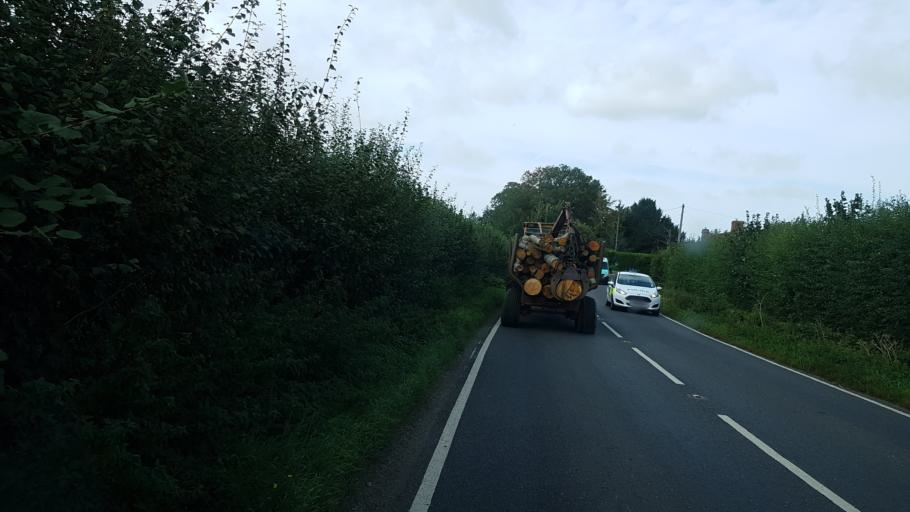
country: GB
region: England
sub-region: Kent
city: Maidstone
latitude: 51.2284
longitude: 0.5496
